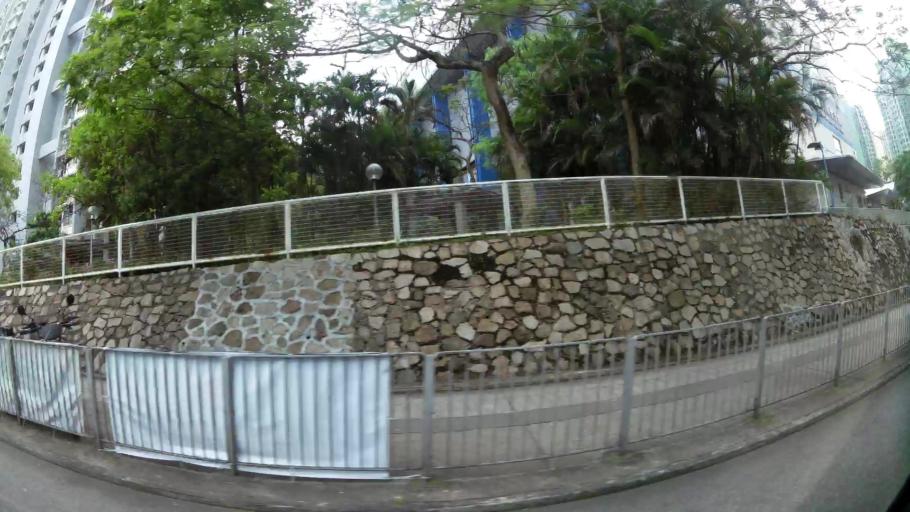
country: HK
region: Kowloon City
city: Kowloon
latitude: 22.3041
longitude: 114.2383
